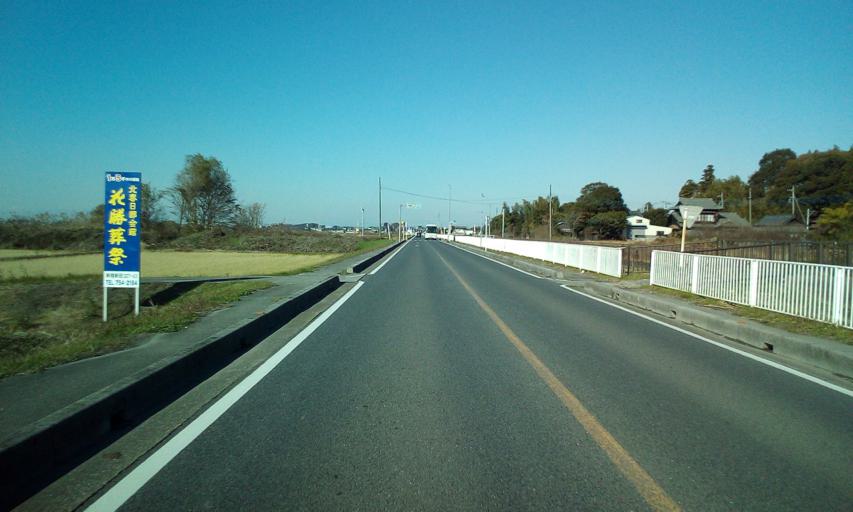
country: JP
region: Chiba
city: Noda
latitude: 35.9592
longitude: 139.8249
